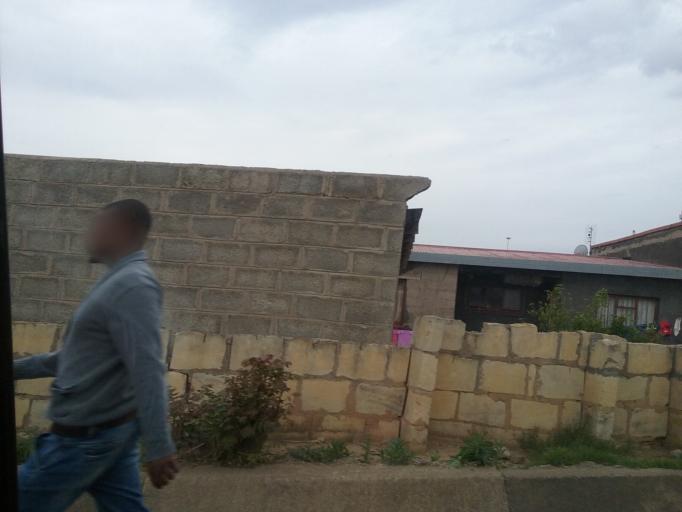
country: LS
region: Maseru
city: Maseru
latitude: -29.3189
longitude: 27.5106
